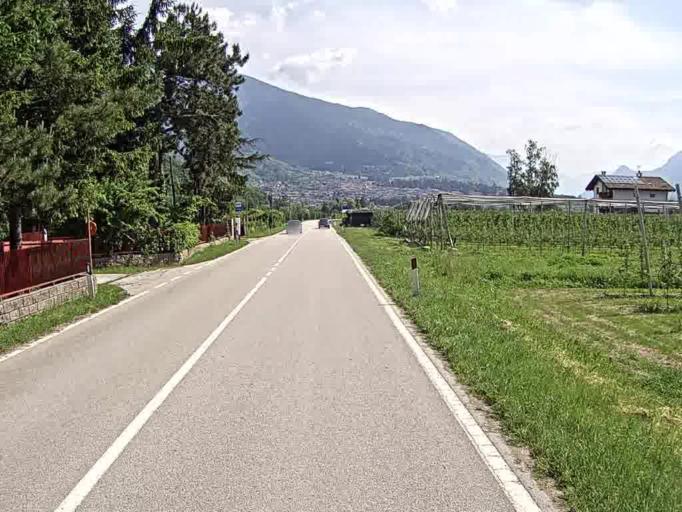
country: IT
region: Trentino-Alto Adige
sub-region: Provincia di Trento
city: Caldonazzo
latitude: 45.9975
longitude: 11.2787
